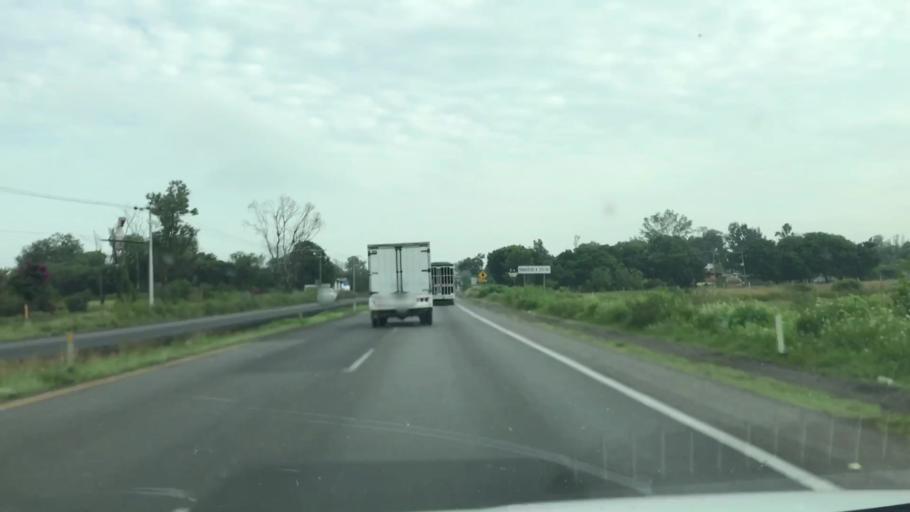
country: MX
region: Guanajuato
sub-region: Irapuato
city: San Ignacio de Rivera (Ojo de Agua)
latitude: 20.5353
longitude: -101.4584
